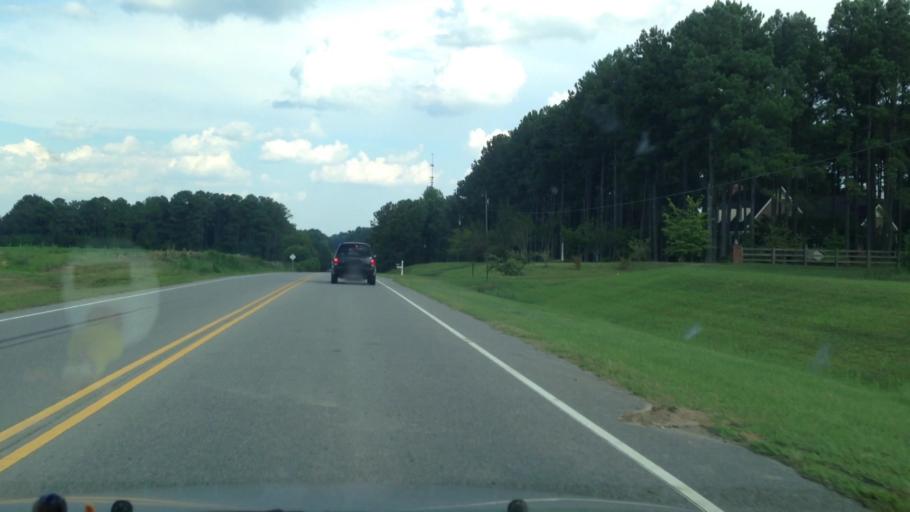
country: US
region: North Carolina
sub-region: Harnett County
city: Lillington
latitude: 35.4130
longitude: -78.8676
